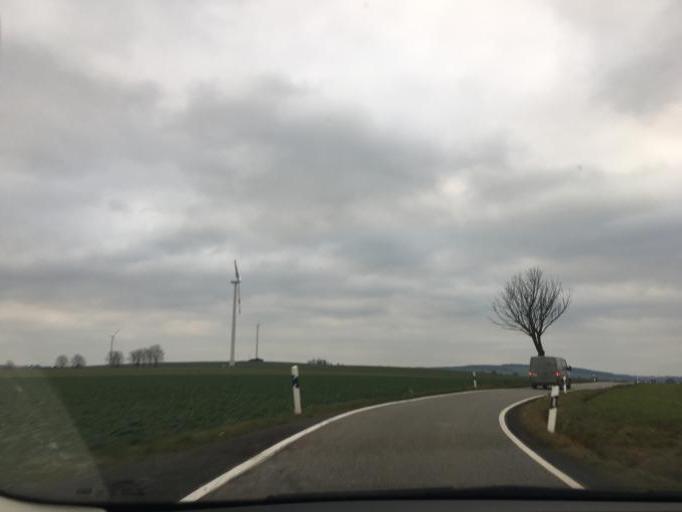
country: DE
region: Saxony
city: Niederfrohna
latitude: 50.8633
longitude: 12.7067
